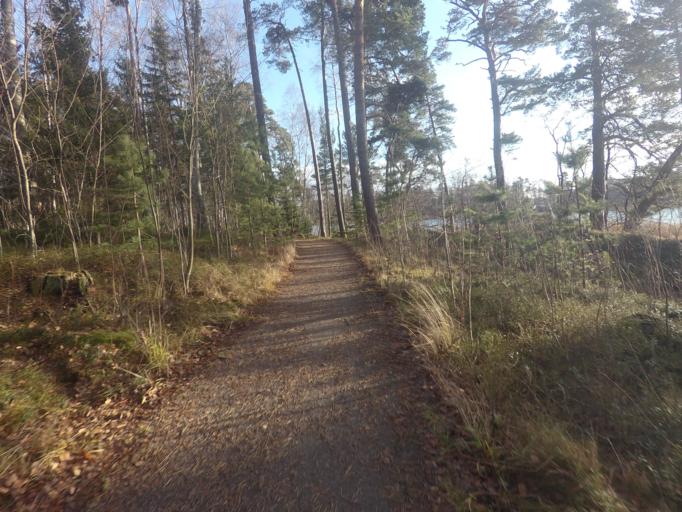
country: FI
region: Uusimaa
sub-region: Helsinki
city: Otaniemi
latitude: 60.1657
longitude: 24.8321
